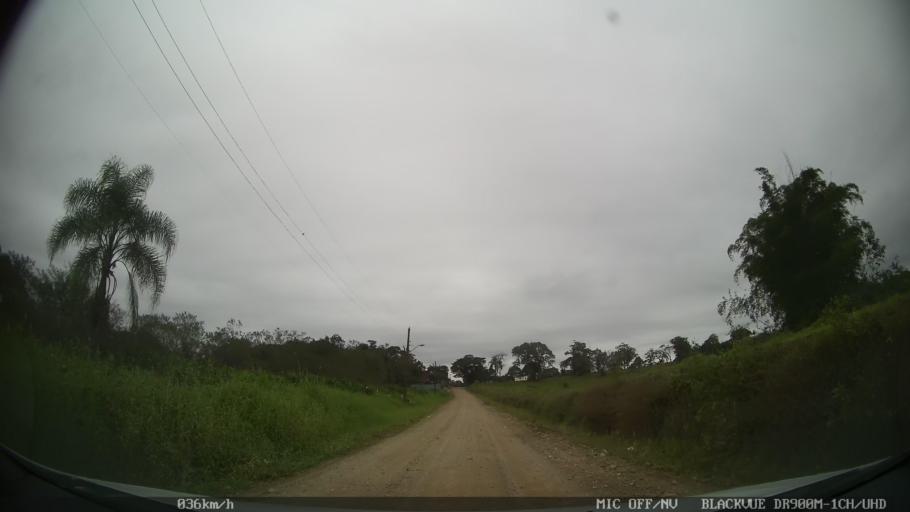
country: BR
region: Santa Catarina
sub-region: Joinville
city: Joinville
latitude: -26.2742
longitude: -48.9094
